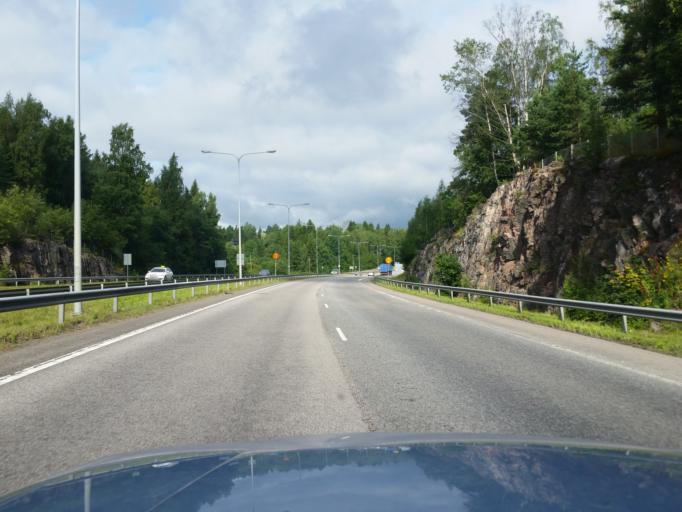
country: FI
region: Uusimaa
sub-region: Helsinki
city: Kauniainen
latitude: 60.2016
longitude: 24.7058
